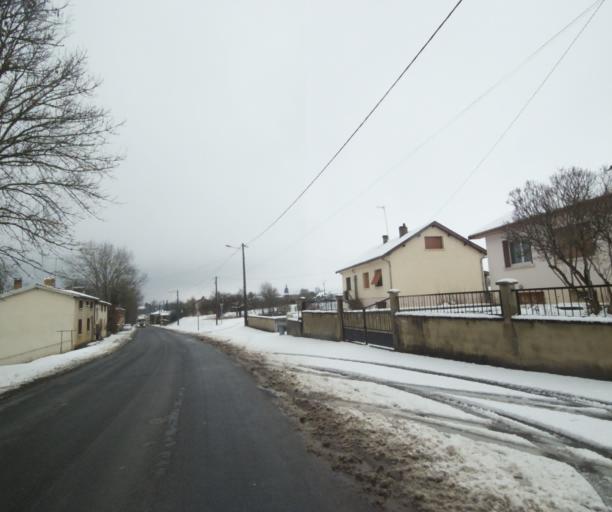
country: FR
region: Champagne-Ardenne
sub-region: Departement de la Haute-Marne
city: Wassy
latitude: 48.4362
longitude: 4.9609
